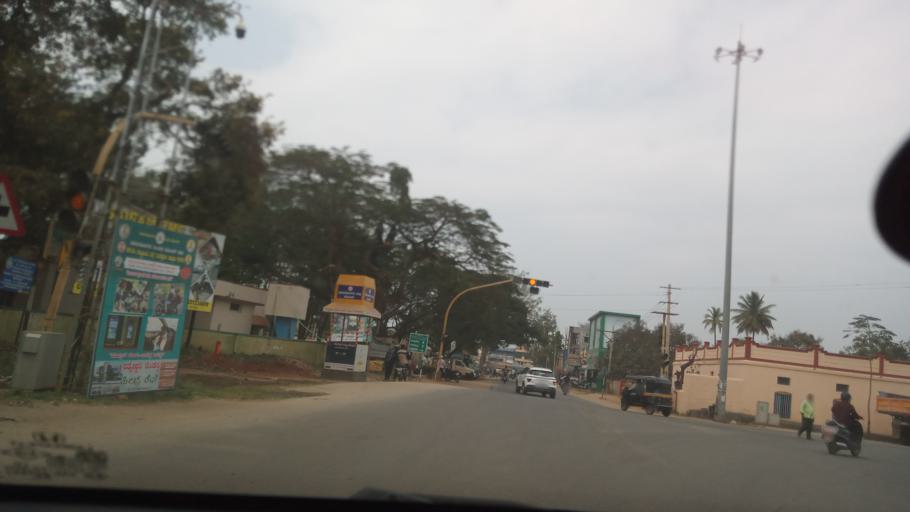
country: IN
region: Karnataka
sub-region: Chamrajnagar
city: Chamrajnagar
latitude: 11.9210
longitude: 76.9386
